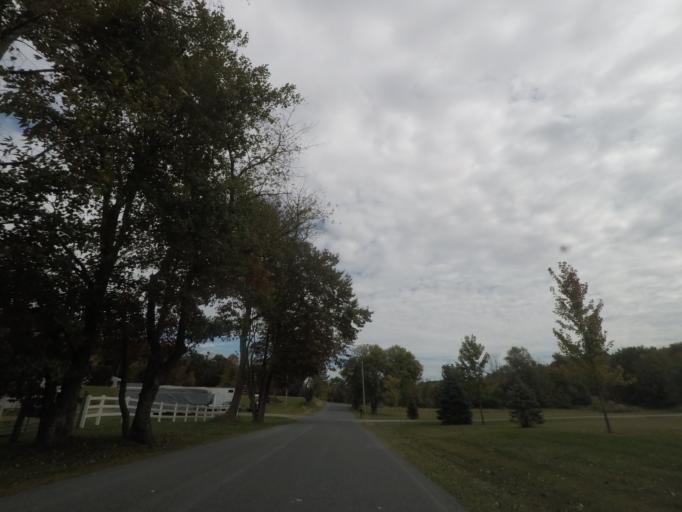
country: US
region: New York
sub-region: Rensselaer County
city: Nassau
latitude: 42.5528
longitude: -73.6507
